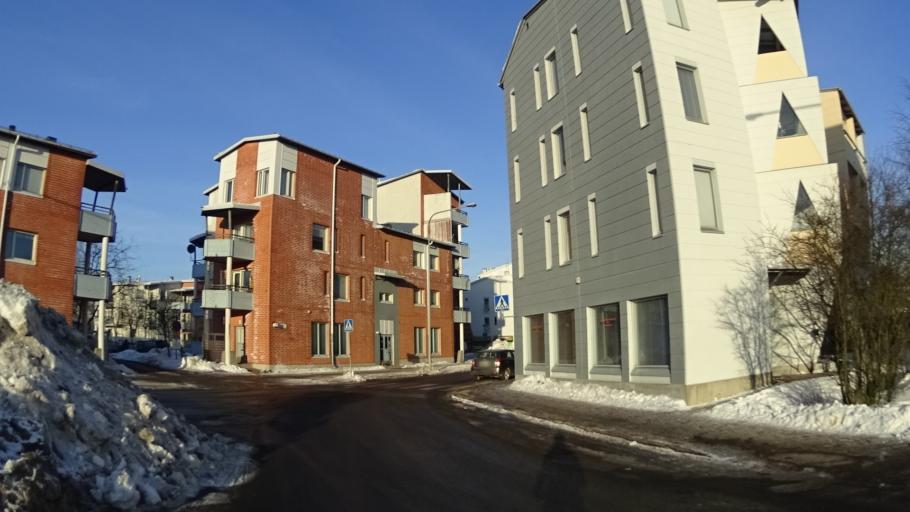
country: FI
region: Uusimaa
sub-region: Helsinki
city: Teekkarikylae
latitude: 60.2072
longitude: 24.8564
